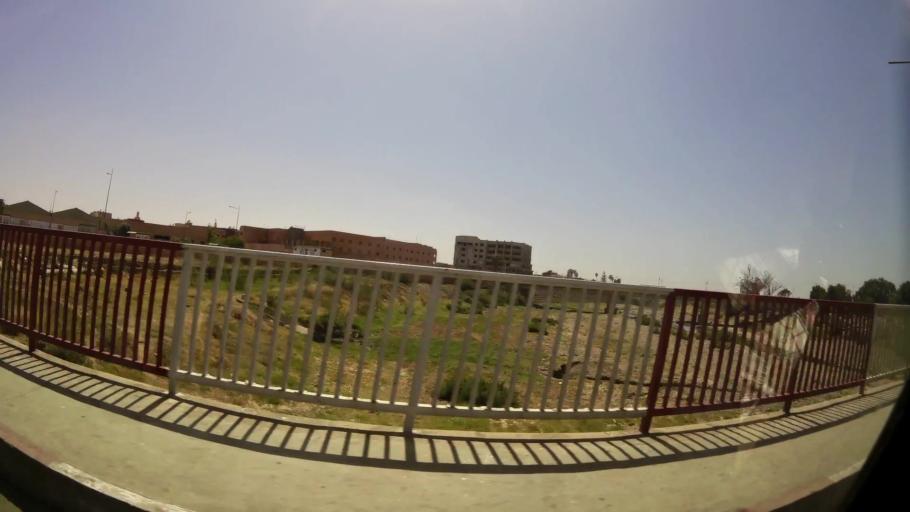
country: MA
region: Souss-Massa-Draa
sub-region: Inezgane-Ait Mellou
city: Inezgane
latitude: 30.3504
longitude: -9.5039
